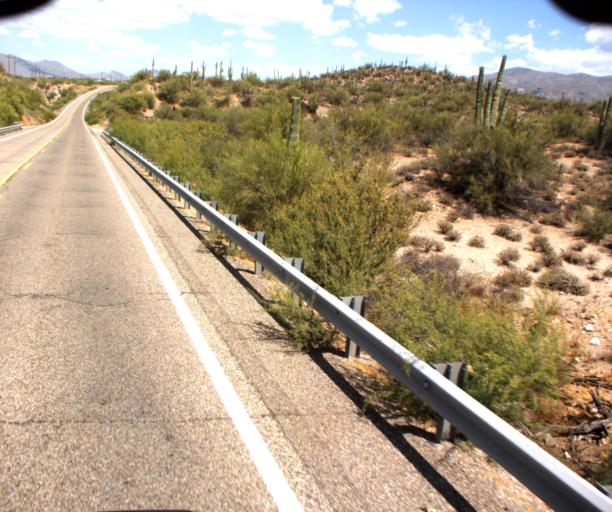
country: US
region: Arizona
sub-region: Pinal County
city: Kearny
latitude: 33.0726
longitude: -110.9188
